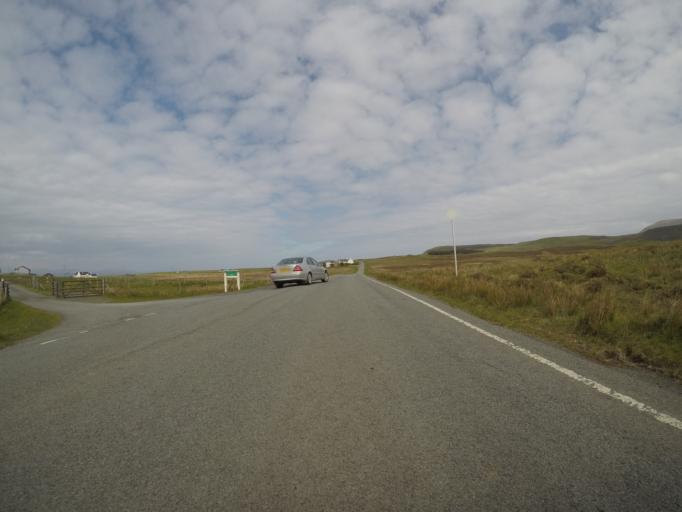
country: GB
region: Scotland
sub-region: Highland
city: Portree
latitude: 57.6549
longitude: -6.3782
